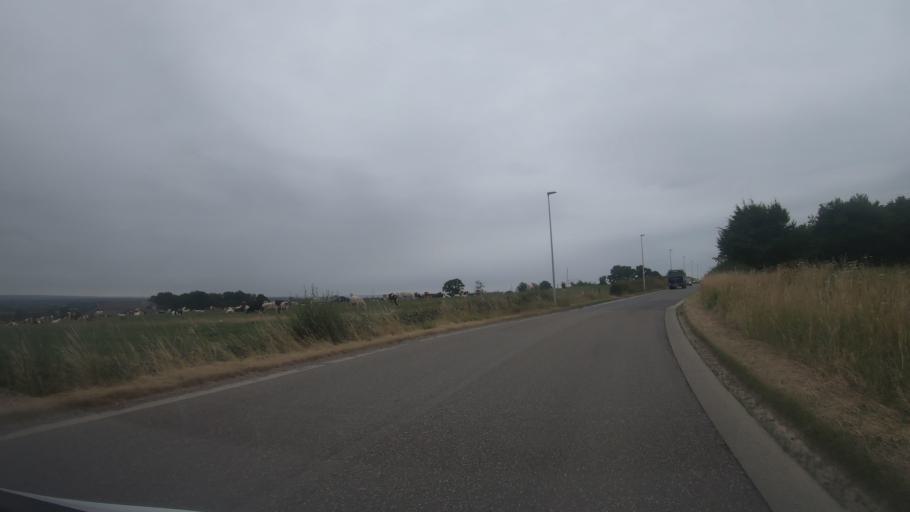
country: BE
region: Wallonia
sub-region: Province de Liege
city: Dison
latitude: 50.6397
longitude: 5.8906
